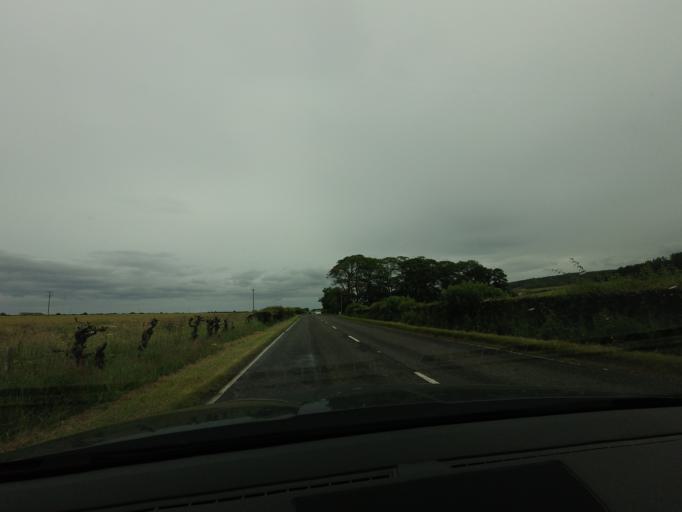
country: GB
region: Scotland
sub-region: Moray
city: Buckie
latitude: 57.6646
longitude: -2.9479
